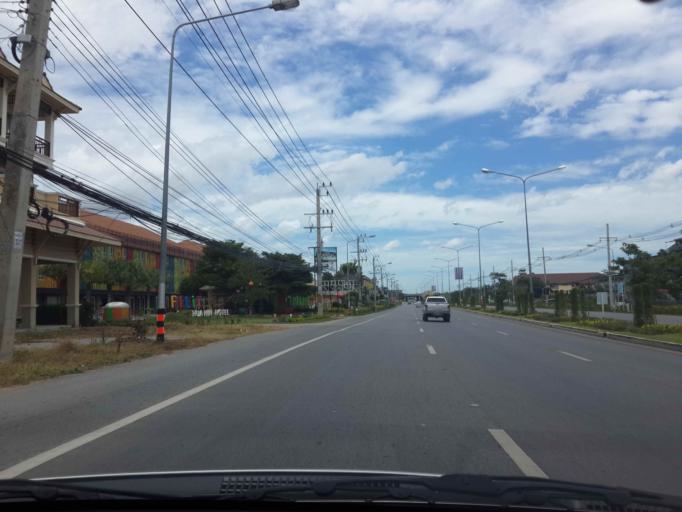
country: TH
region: Prachuap Khiri Khan
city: Hua Hin
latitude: 12.6359
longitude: 99.9484
